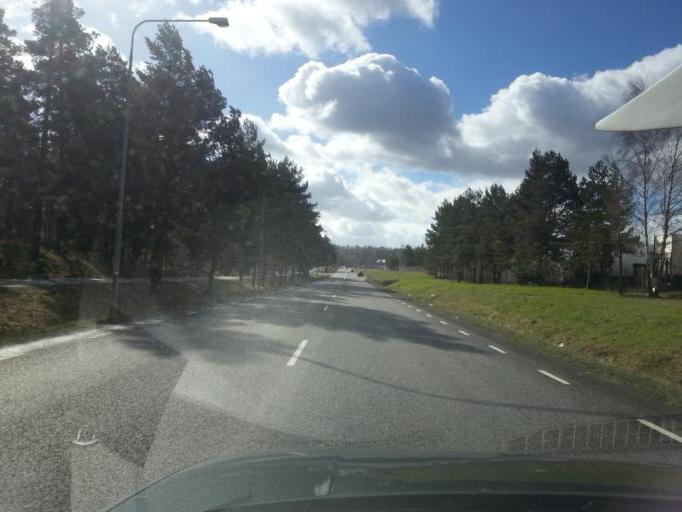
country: SE
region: Joenkoeping
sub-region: Jonkopings Kommun
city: Jonkoping
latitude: 57.7510
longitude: 14.1721
